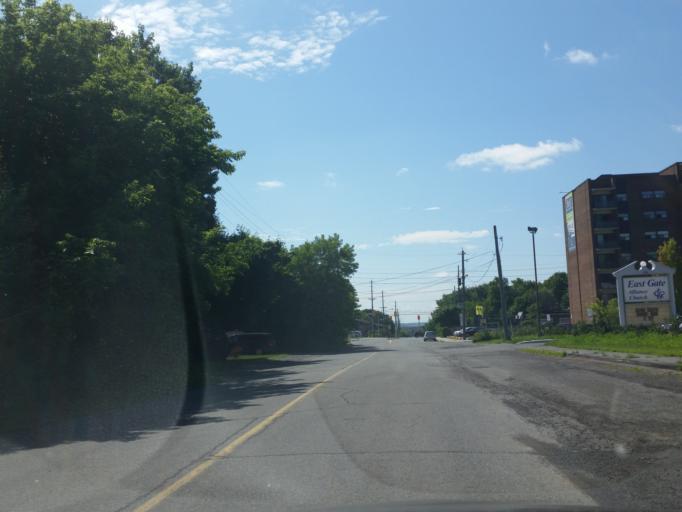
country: CA
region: Quebec
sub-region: Outaouais
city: Gatineau
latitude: 45.4478
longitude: -75.6321
